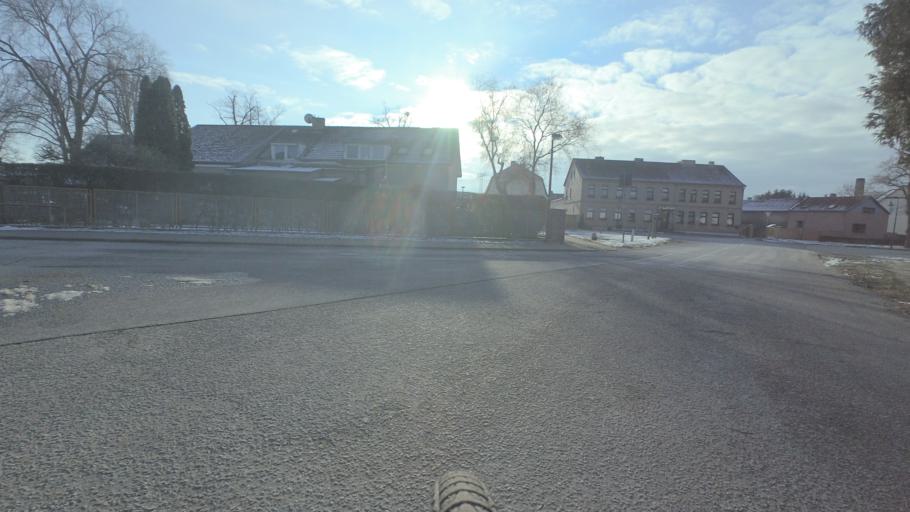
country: DE
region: Brandenburg
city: Zossen
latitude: 52.2262
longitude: 13.4160
